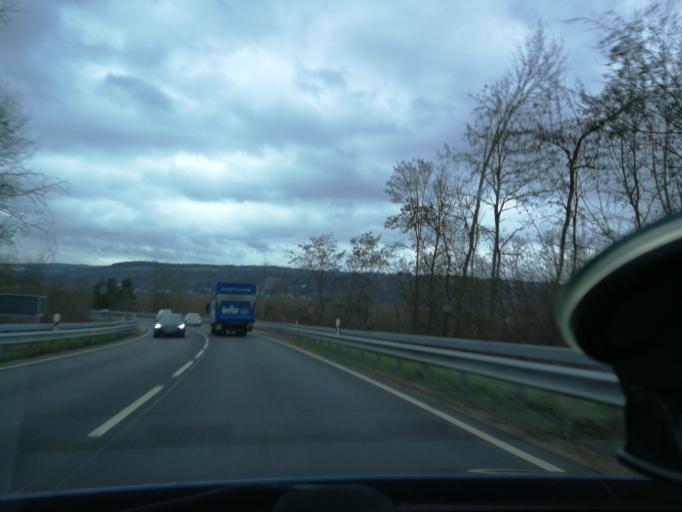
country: DE
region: Rheinland-Pfalz
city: Konz
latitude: 49.7123
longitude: 6.5723
